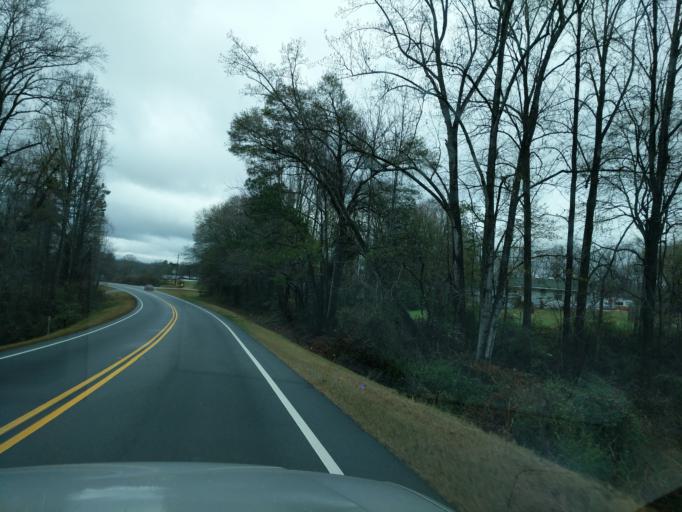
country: US
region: Georgia
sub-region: Franklin County
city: Lavonia
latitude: 34.3749
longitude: -83.0852
